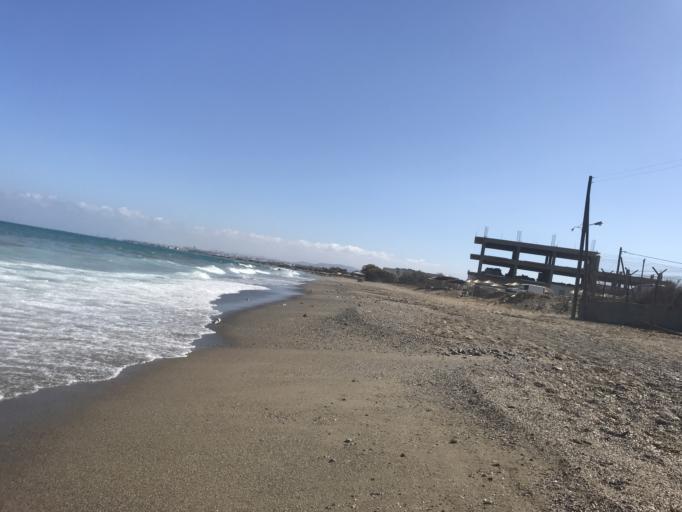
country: GR
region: Crete
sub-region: Nomos Irakleiou
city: Gazi
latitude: 35.3416
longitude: 25.0542
